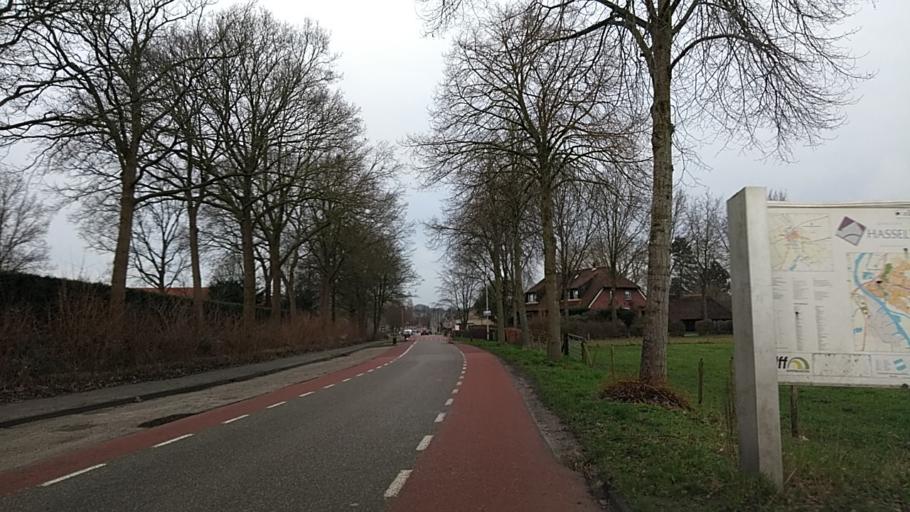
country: NL
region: Overijssel
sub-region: Gemeente Zwartewaterland
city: Hasselt
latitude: 52.5884
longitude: 6.1066
